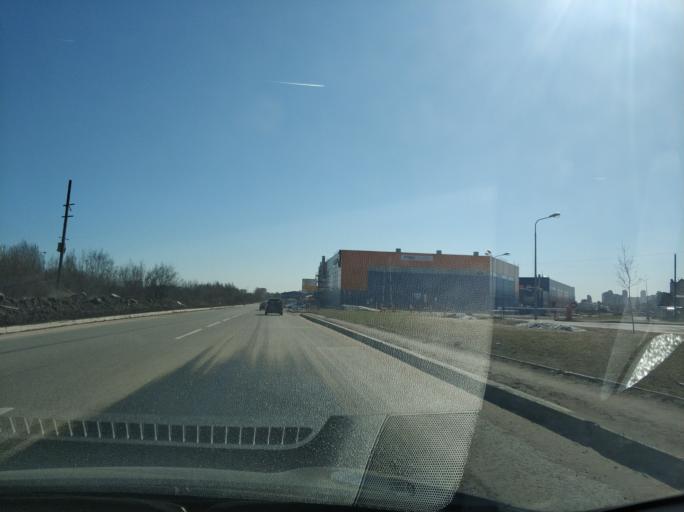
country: RU
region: Leningrad
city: Bugry
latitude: 60.0691
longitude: 30.3812
